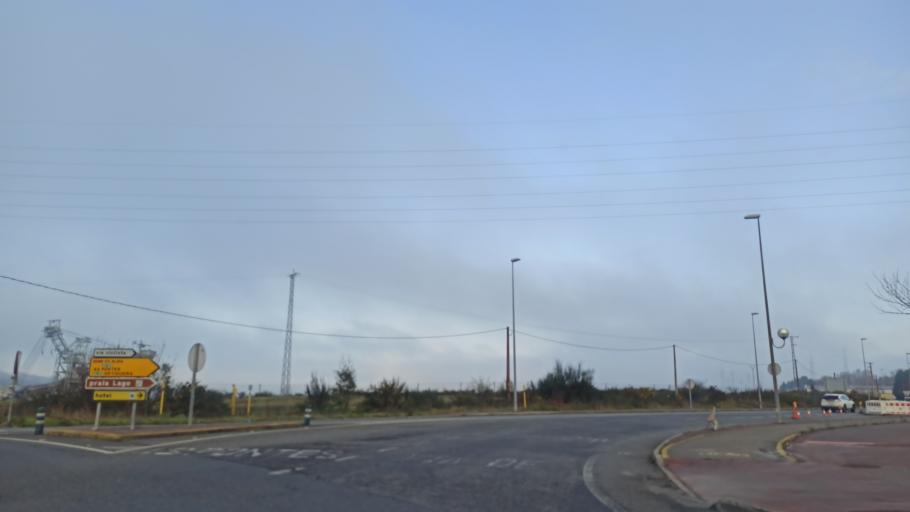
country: ES
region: Galicia
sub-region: Provincia da Coruna
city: As Pontes de Garcia Rodriguez
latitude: 43.4427
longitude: -7.8668
